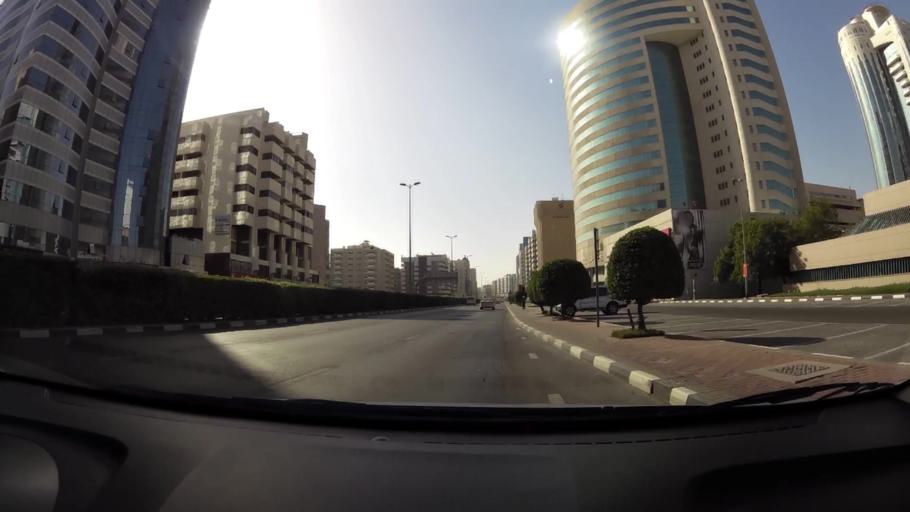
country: AE
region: Ash Shariqah
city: Sharjah
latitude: 25.2640
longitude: 55.3150
